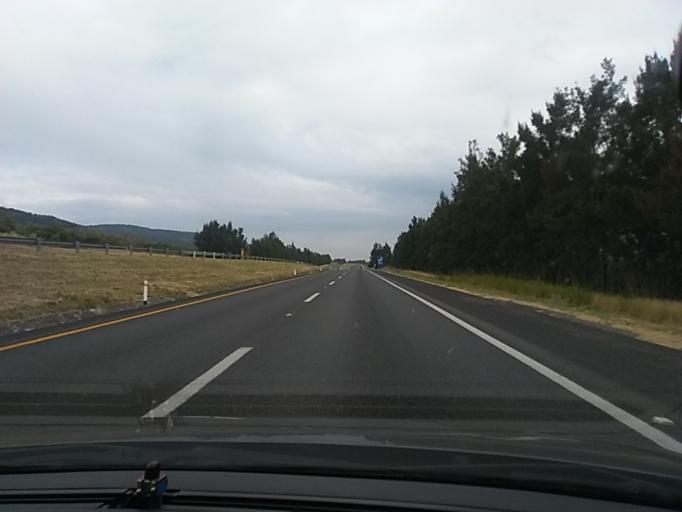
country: MX
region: Michoacan
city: Churintzio
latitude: 20.1088
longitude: -102.0386
